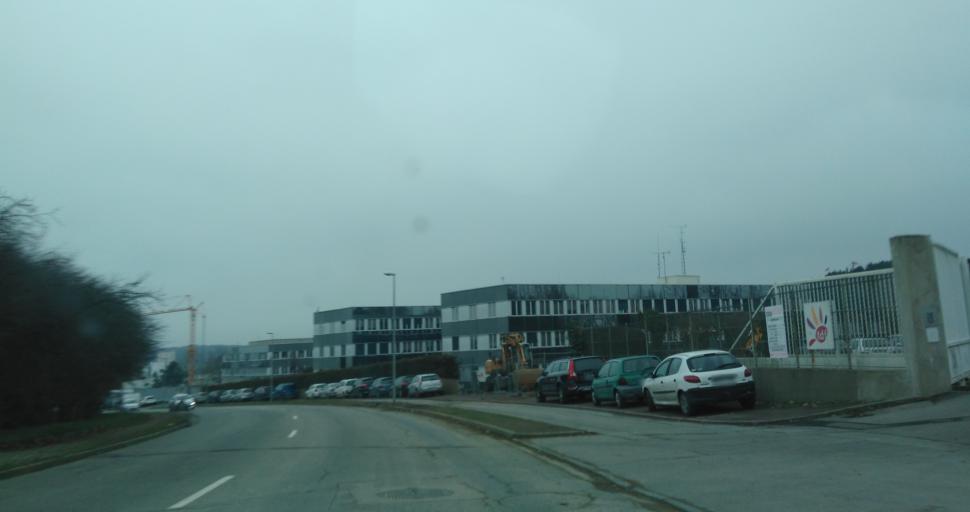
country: FR
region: Brittany
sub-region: Departement d'Ille-et-Vilaine
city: Cesson-Sevigne
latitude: 48.1247
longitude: -1.6280
